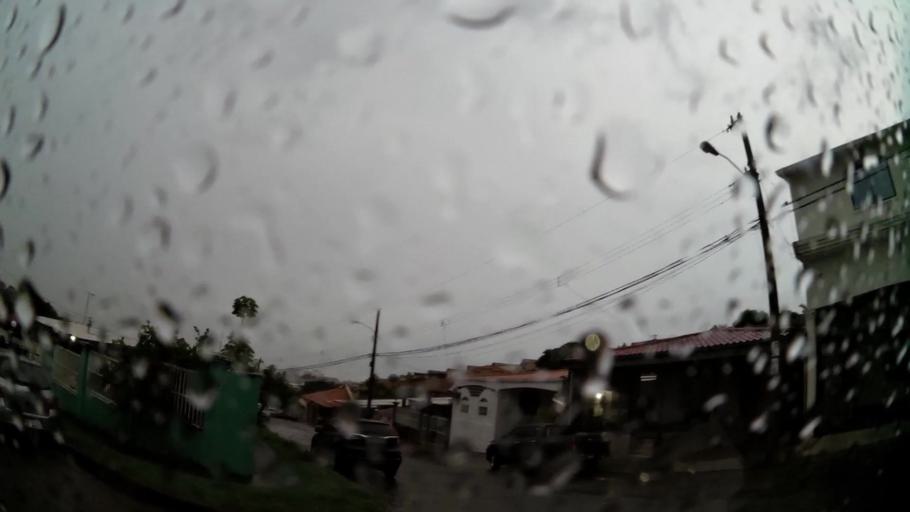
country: PA
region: Panama
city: San Miguelito
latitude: 9.0572
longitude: -79.4769
